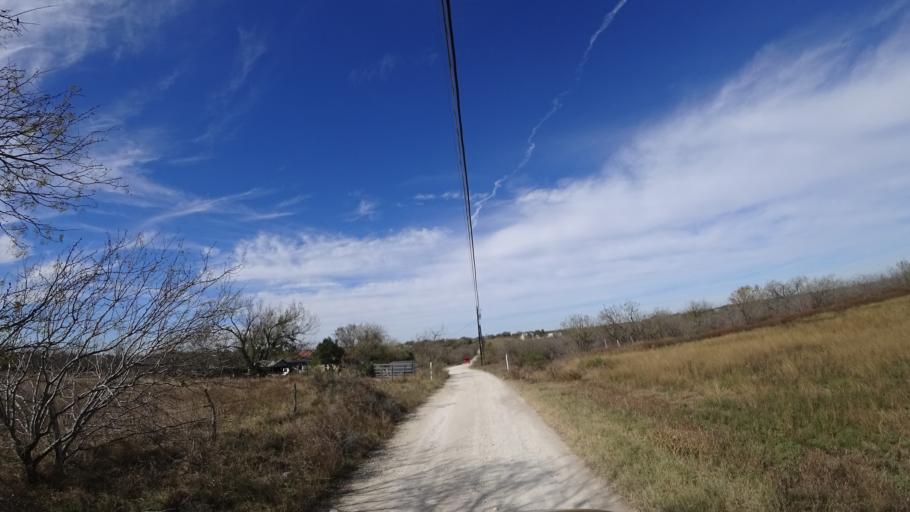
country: US
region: Texas
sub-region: Travis County
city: Onion Creek
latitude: 30.1167
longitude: -97.6843
